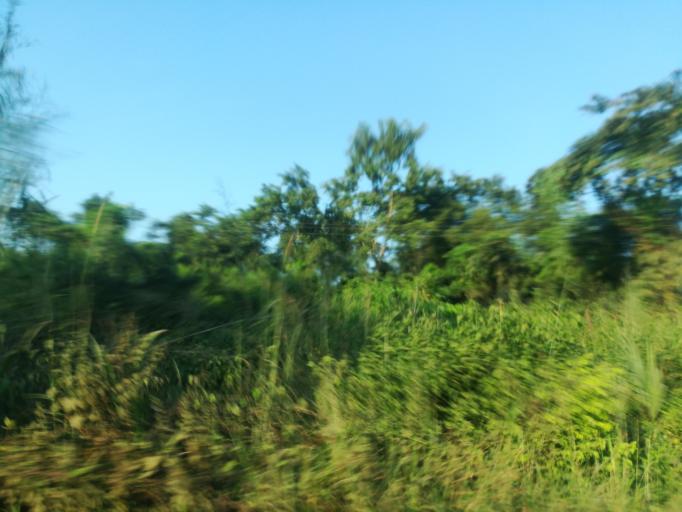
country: NG
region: Ogun
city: Abeokuta
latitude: 7.2045
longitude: 3.2126
